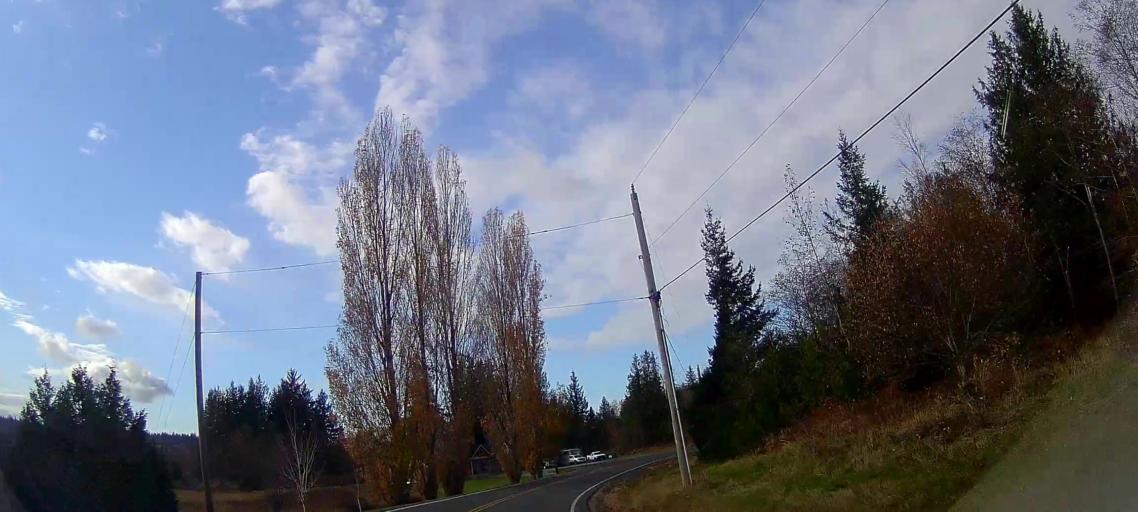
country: US
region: Washington
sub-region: Skagit County
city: Big Lake
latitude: 48.4170
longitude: -122.2337
